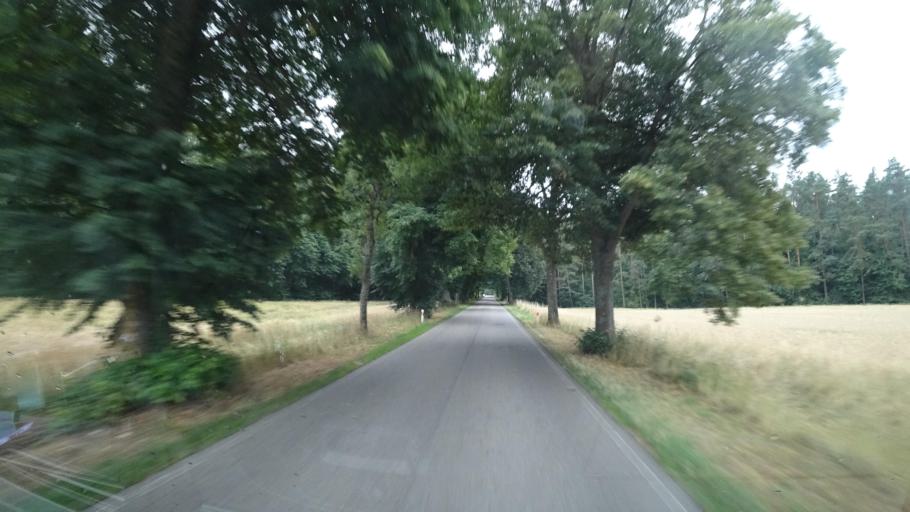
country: PL
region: Warmian-Masurian Voivodeship
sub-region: Powiat gizycki
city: Ryn
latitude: 53.8929
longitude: 21.5739
